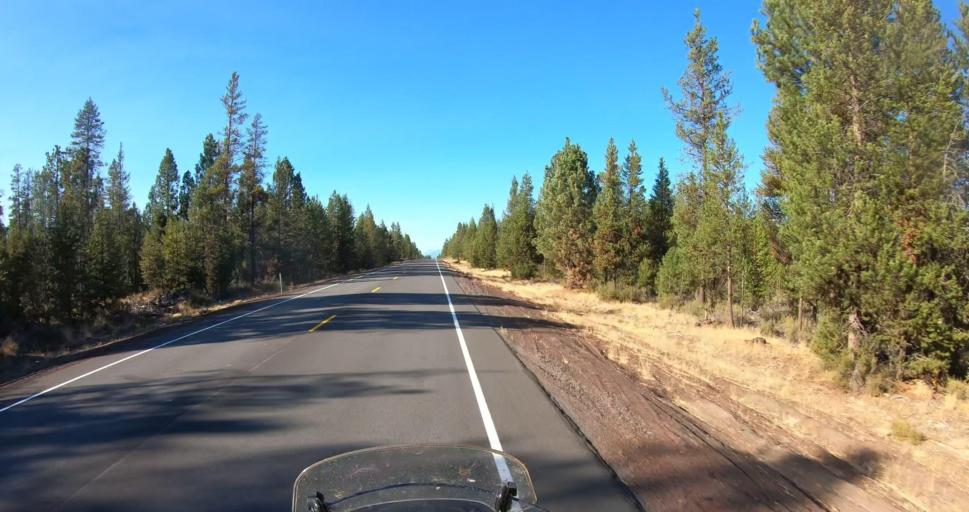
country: US
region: Oregon
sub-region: Deschutes County
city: La Pine
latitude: 43.5405
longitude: -121.4663
